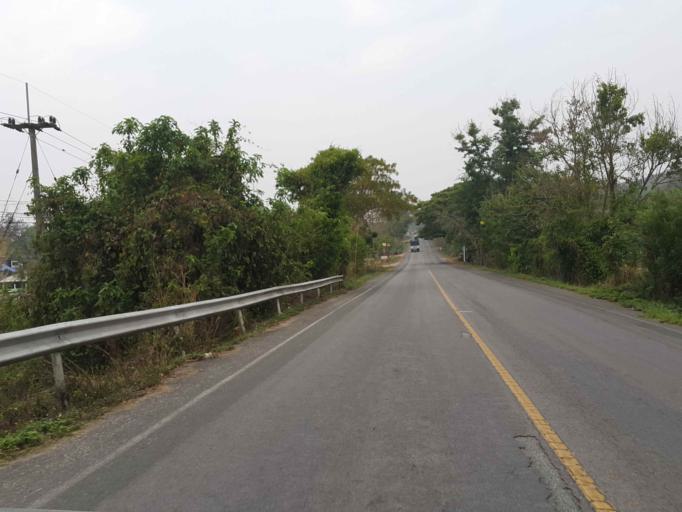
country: TH
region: Chiang Mai
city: Mae Taeng
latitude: 19.1013
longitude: 98.9998
